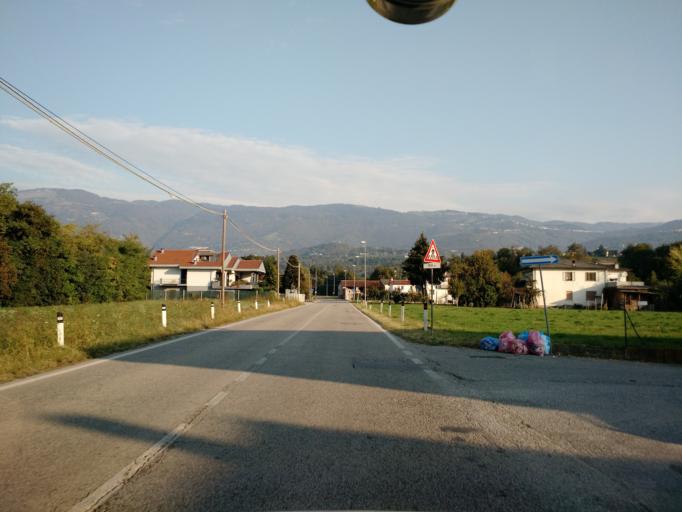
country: IT
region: Veneto
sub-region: Provincia di Vicenza
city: Fara Vicentino
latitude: 45.7319
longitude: 11.5421
